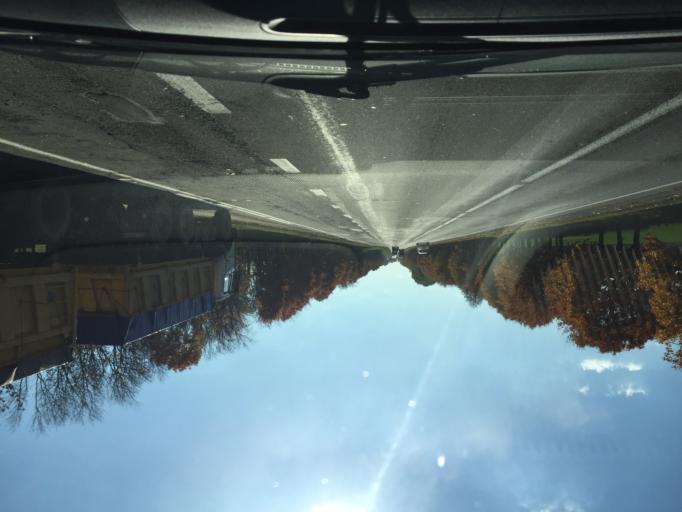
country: BY
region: Minsk
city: Salihorsk
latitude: 52.8910
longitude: 27.4722
